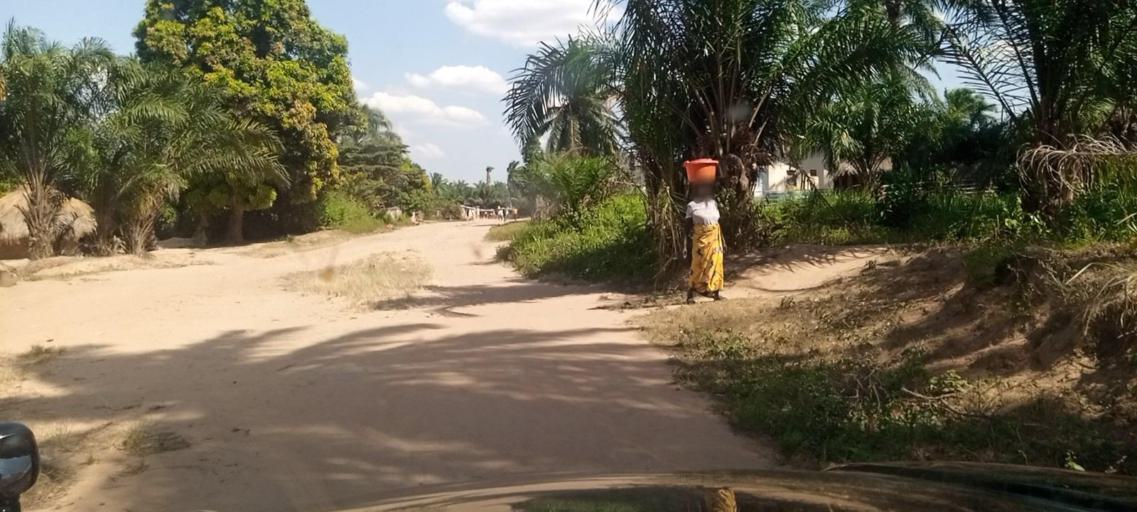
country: CD
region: Kasai-Oriental
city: Kabinda
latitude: -6.1283
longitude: 24.5265
